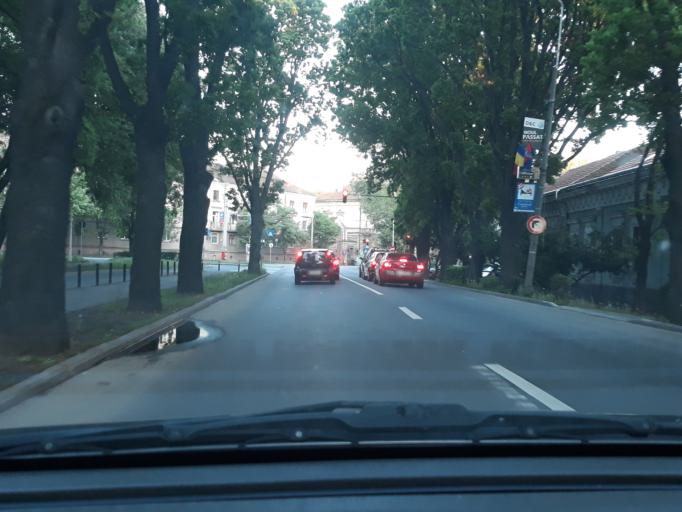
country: RO
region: Bihor
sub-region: Comuna Biharea
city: Oradea
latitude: 47.0645
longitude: 21.9365
